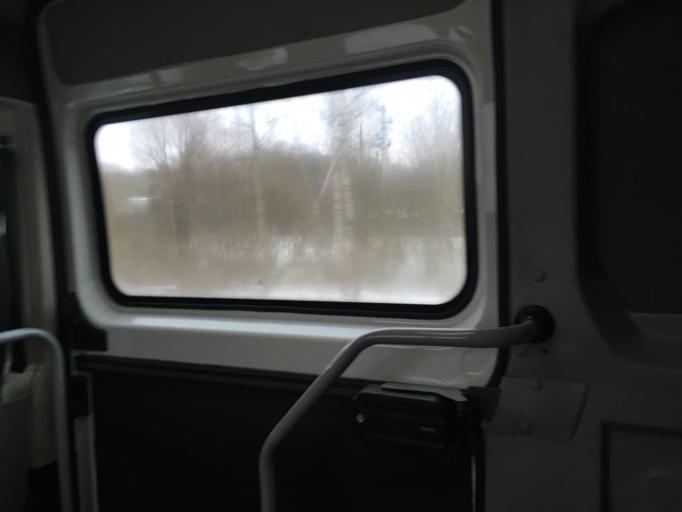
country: RU
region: Tula
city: Krapivna
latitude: 54.1366
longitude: 37.2824
